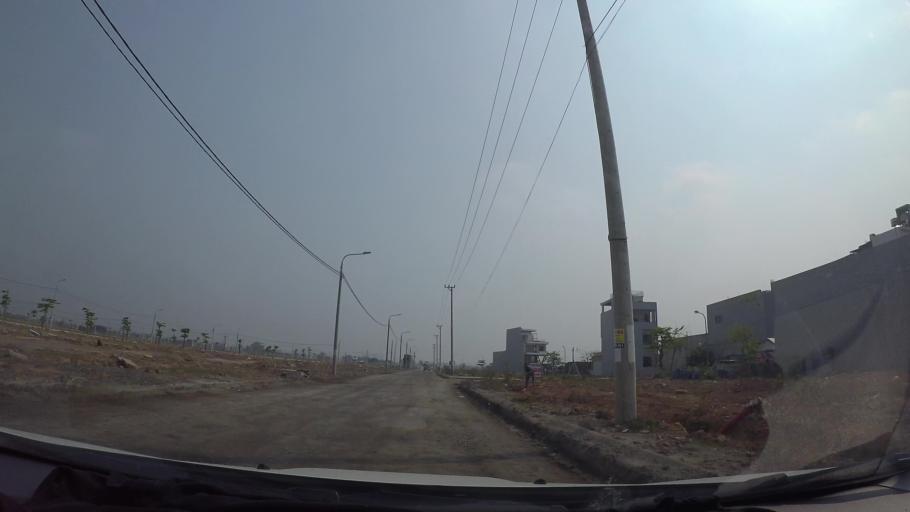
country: VN
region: Da Nang
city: Ngu Hanh Son
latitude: 16.0001
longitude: 108.2344
